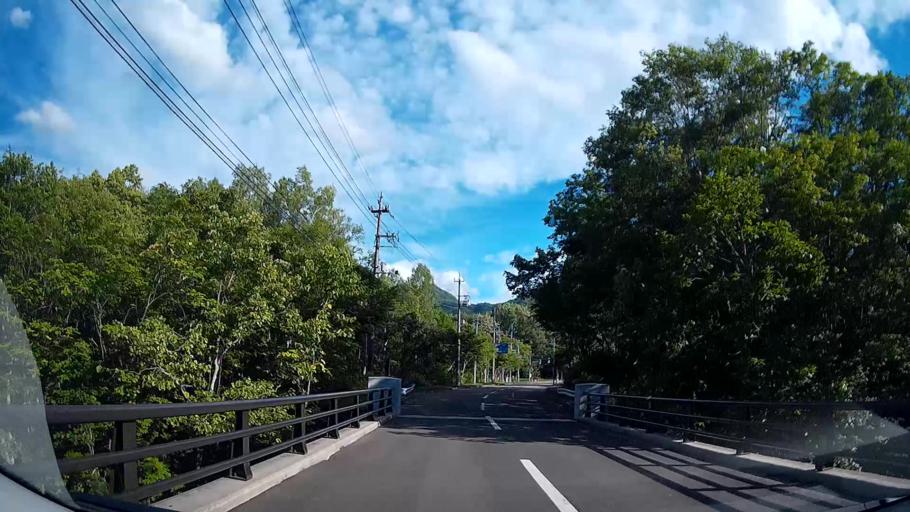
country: JP
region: Hokkaido
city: Sapporo
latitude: 42.9740
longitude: 141.1660
